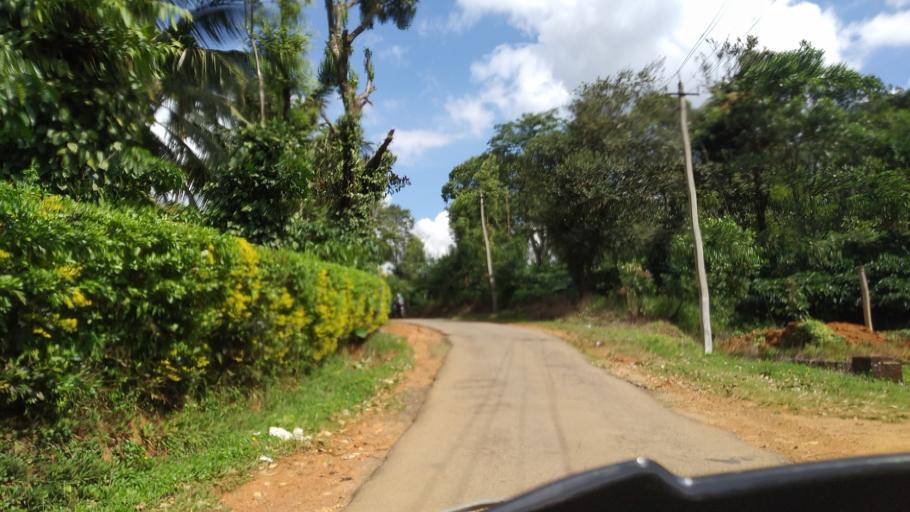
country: IN
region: Karnataka
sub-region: Kodagu
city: Ponnampet
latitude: 12.0309
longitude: 75.8983
